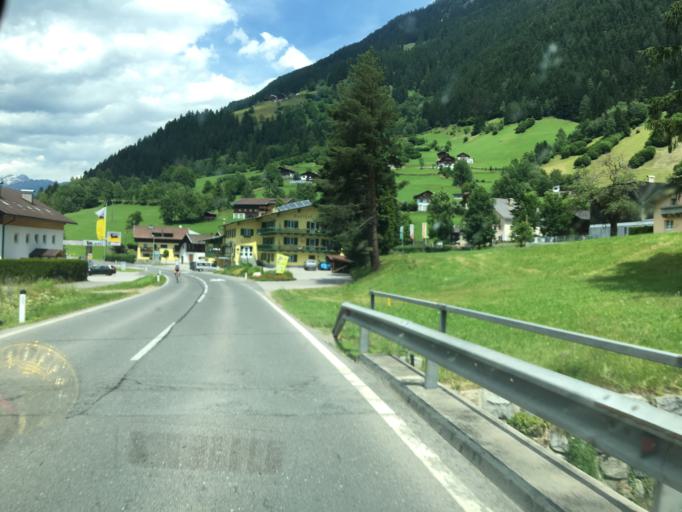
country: AT
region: Carinthia
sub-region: Politischer Bezirk Spittal an der Drau
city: Mortschach
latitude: 46.9212
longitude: 12.9109
